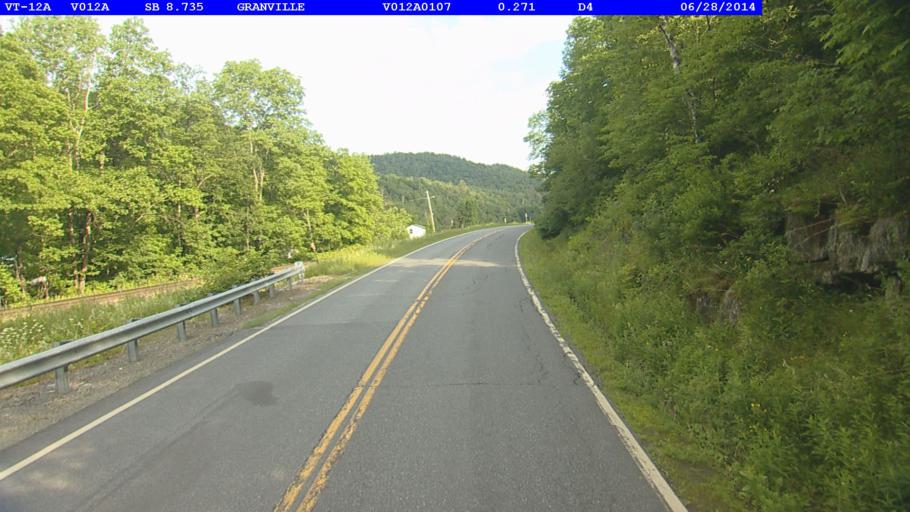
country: US
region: Vermont
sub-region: Orange County
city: Randolph
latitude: 44.0145
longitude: -72.7567
